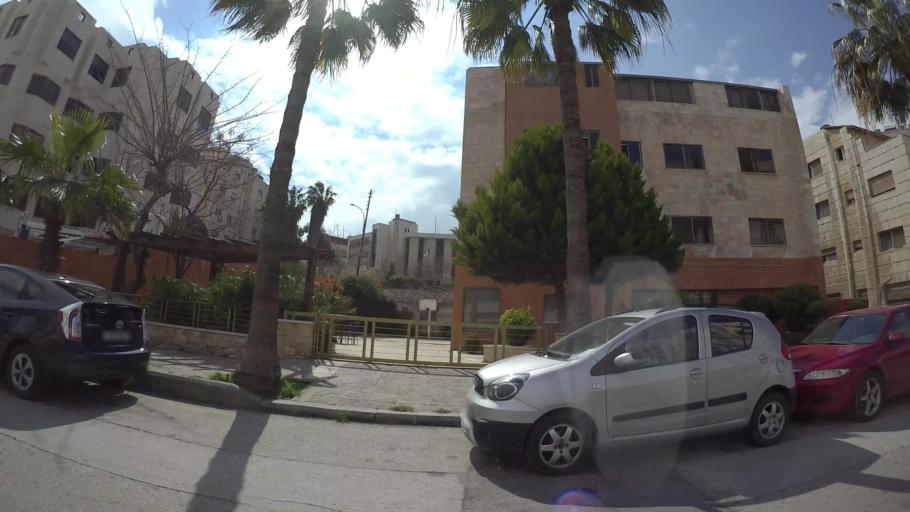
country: JO
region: Amman
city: Amman
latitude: 31.9780
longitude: 35.8968
